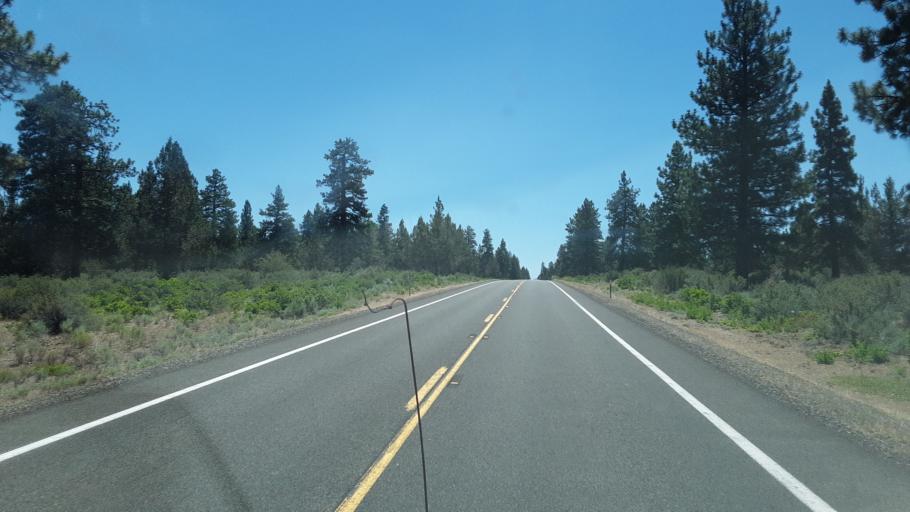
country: US
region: California
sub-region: Siskiyou County
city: Tulelake
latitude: 41.6202
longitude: -121.2193
